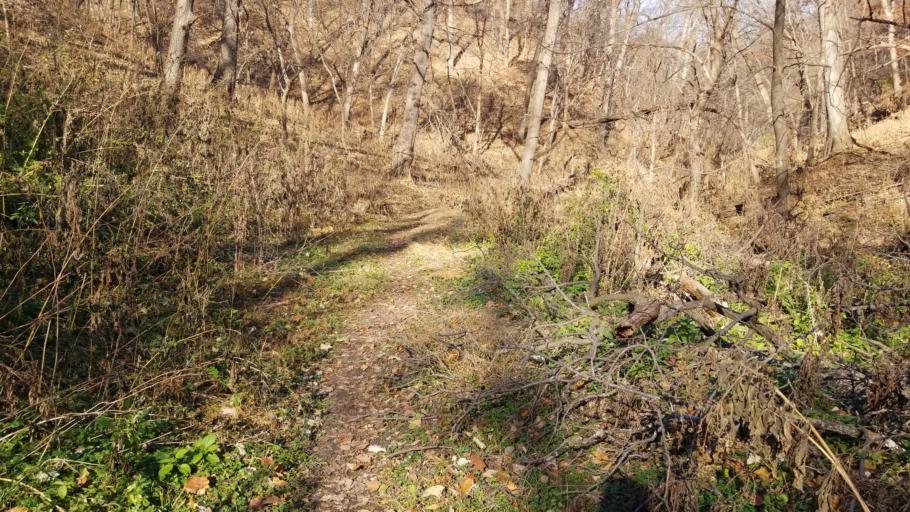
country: US
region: Nebraska
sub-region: Sarpy County
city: Bellevue
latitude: 41.1640
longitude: -95.8948
